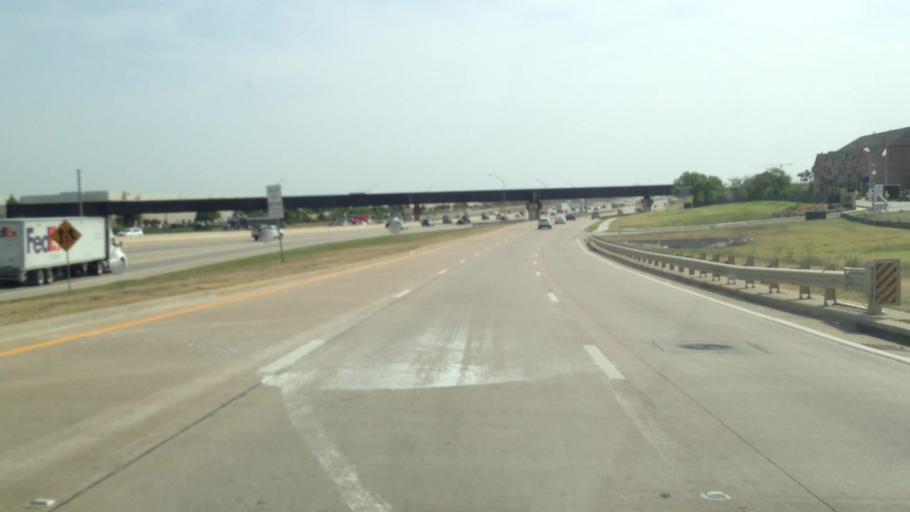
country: US
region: Texas
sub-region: Denton County
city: The Colony
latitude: 33.0522
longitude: -96.9170
